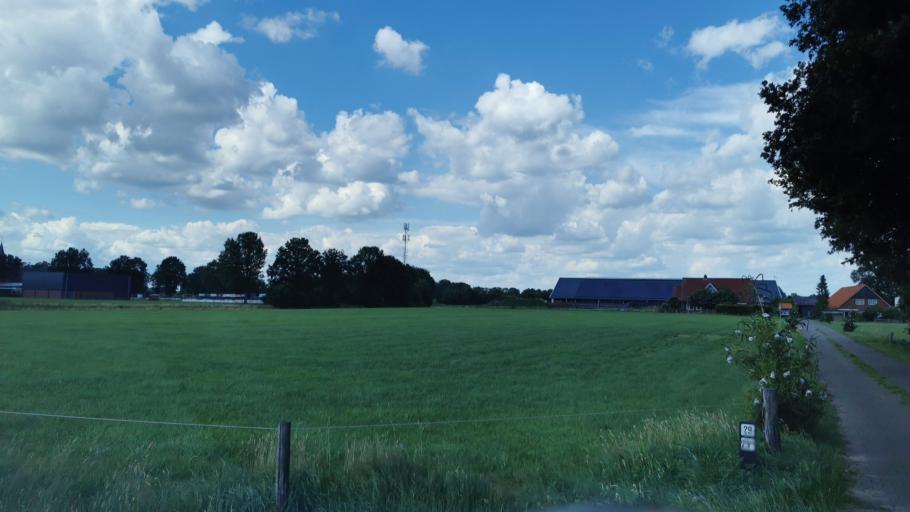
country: DE
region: Lower Saxony
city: Lage
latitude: 52.4240
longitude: 6.9800
